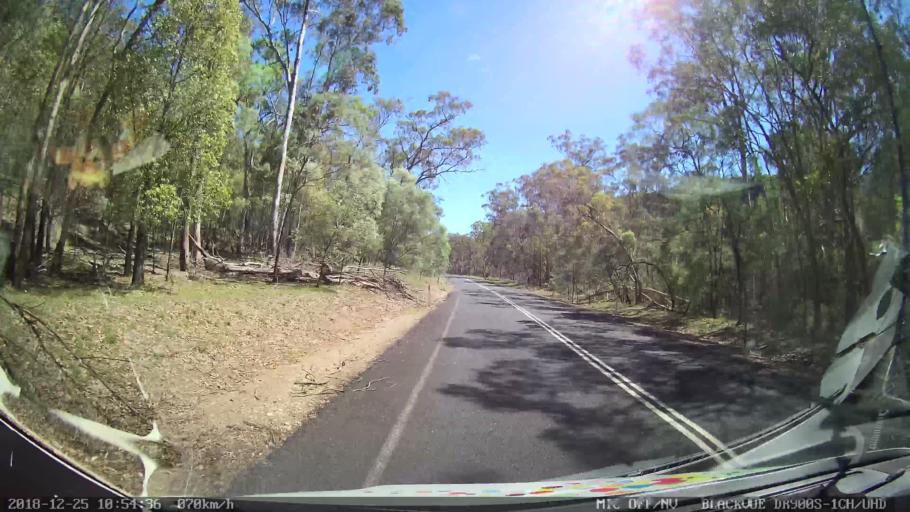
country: AU
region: New South Wales
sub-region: Upper Hunter Shire
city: Merriwa
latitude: -32.4081
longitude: 150.2735
